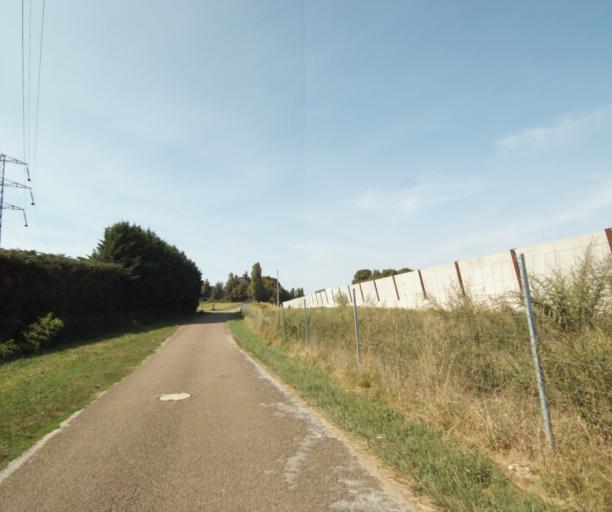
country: FR
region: Bourgogne
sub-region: Departement de Saone-et-Loire
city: Tournus
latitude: 46.5561
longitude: 4.9003
